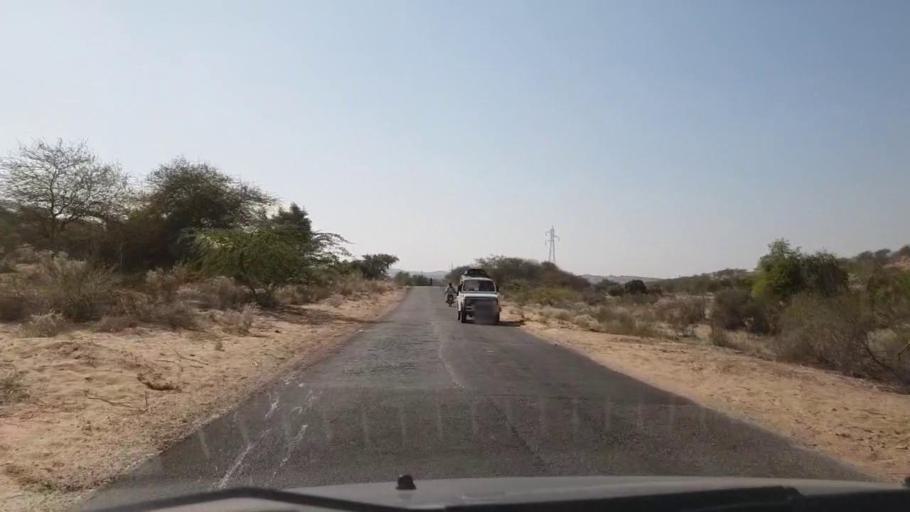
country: PK
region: Sindh
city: Mithi
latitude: 24.6708
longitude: 69.7671
